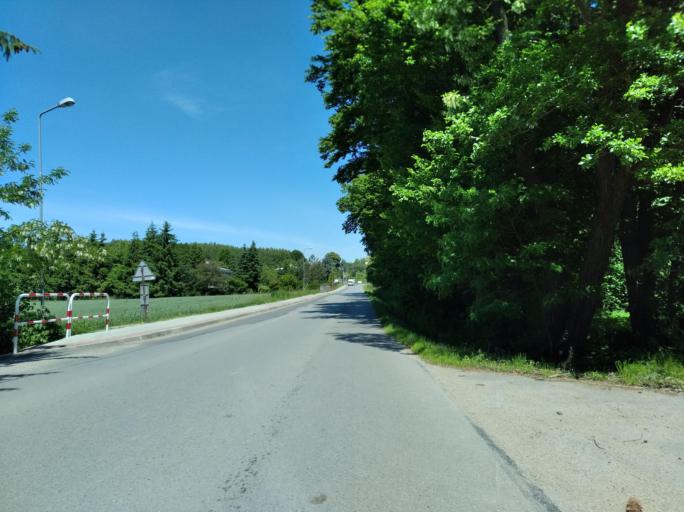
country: PL
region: Subcarpathian Voivodeship
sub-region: Powiat jasielski
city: Tarnowiec
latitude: 49.7377
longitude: 21.5813
